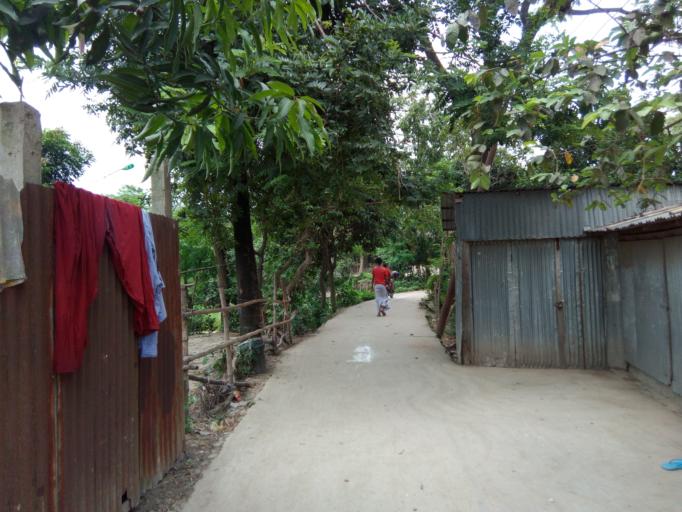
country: BD
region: Dhaka
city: Paltan
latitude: 23.7543
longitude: 90.4869
